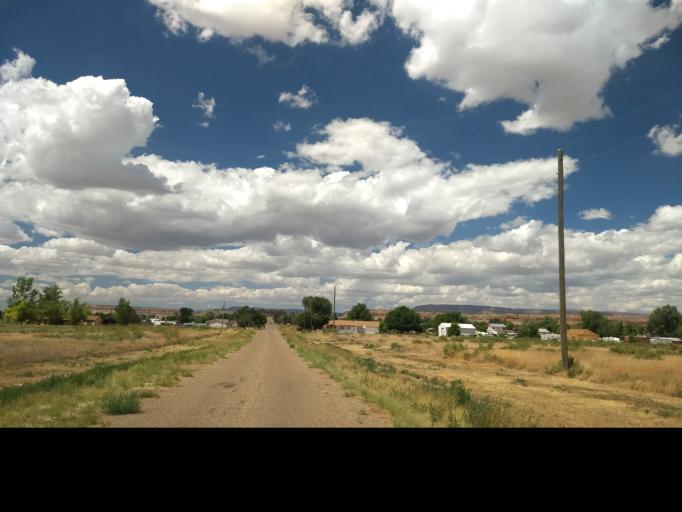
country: US
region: Arizona
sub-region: Coconino County
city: Fredonia
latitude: 36.9456
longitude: -112.5159
